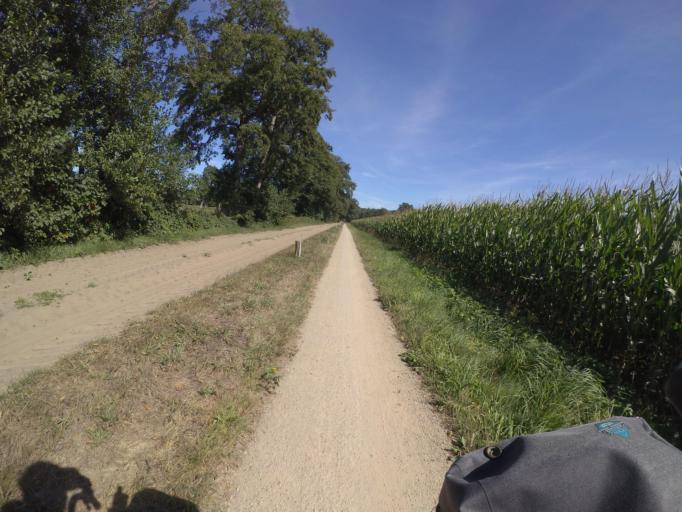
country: NL
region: Overijssel
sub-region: Gemeente Twenterand
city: Den Ham
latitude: 52.4195
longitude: 6.4326
